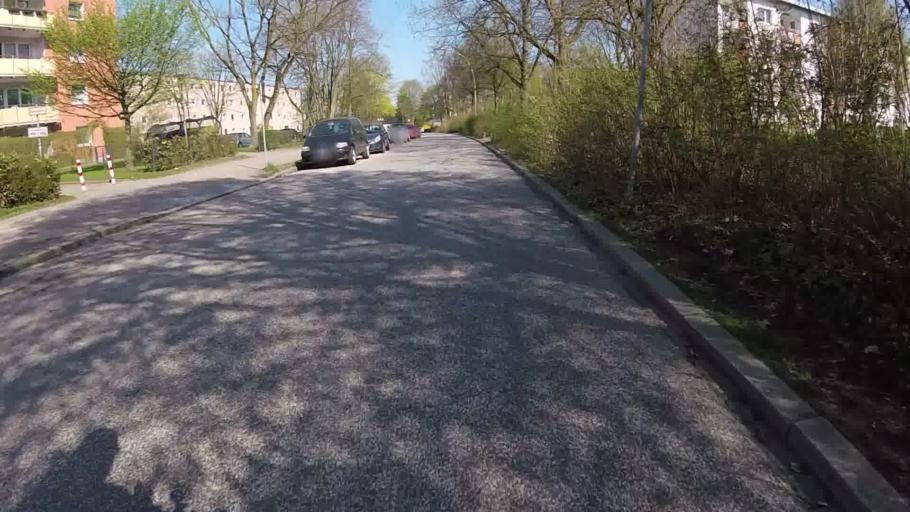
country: DE
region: Hamburg
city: Farmsen-Berne
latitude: 53.5879
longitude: 10.1415
